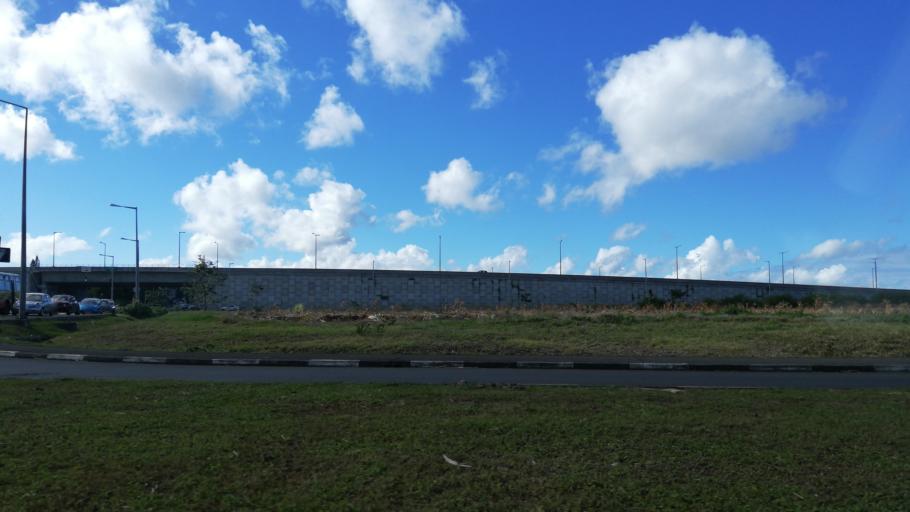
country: MU
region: Moka
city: Verdun
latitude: -20.2282
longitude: 57.5436
